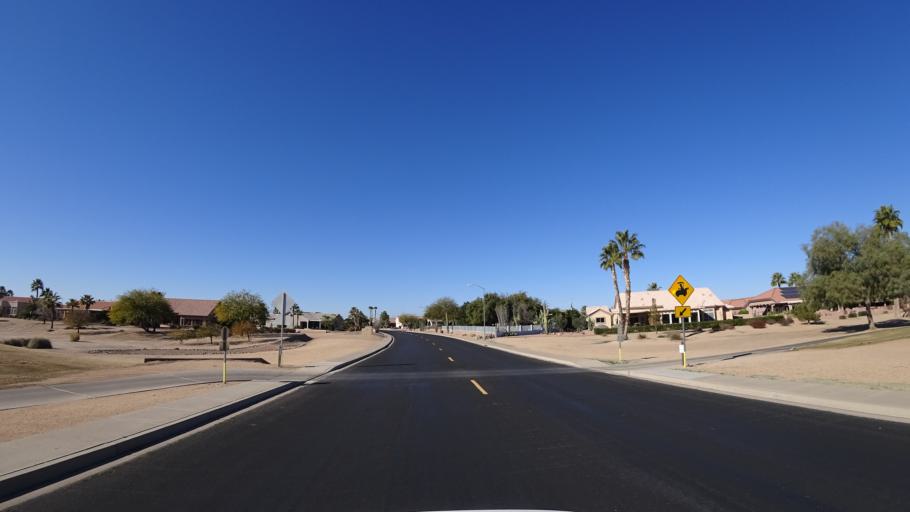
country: US
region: Arizona
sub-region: Maricopa County
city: Sun City West
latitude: 33.6916
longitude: -112.3691
